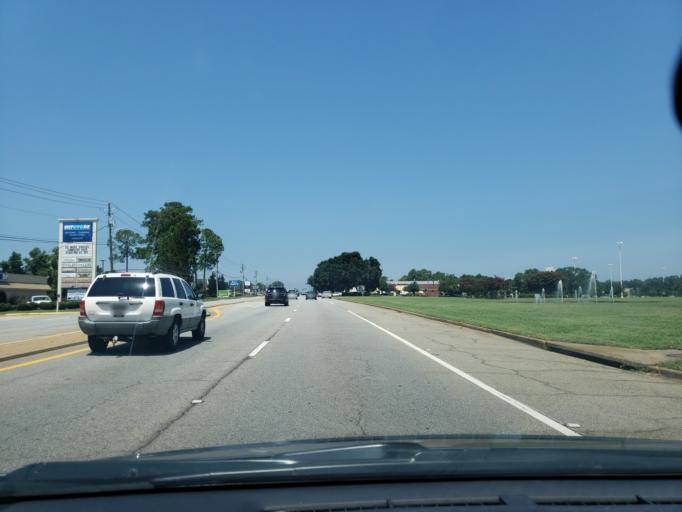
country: US
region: Georgia
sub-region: Dougherty County
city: Albany
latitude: 31.6153
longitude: -84.2183
